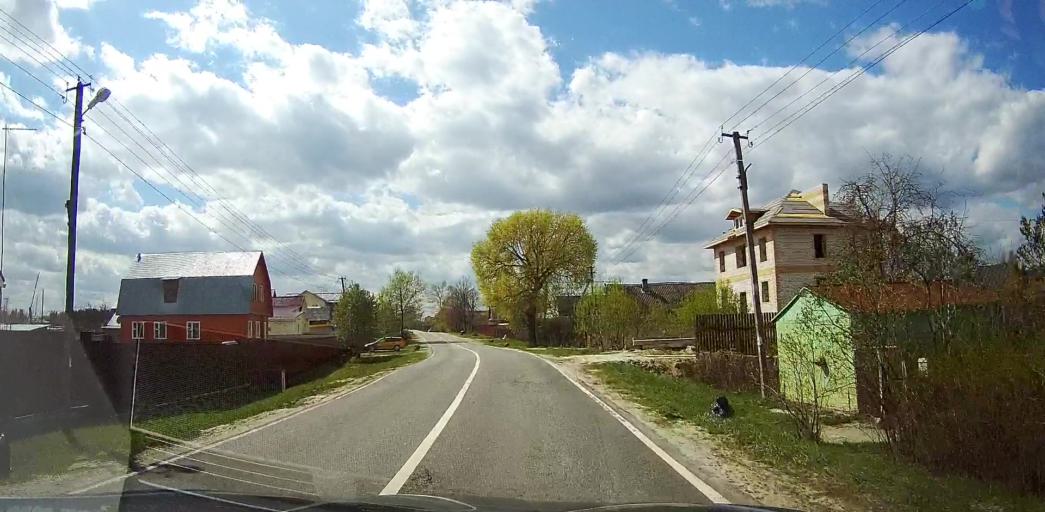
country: RU
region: Moskovskaya
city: Davydovo
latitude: 55.5567
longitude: 38.8228
